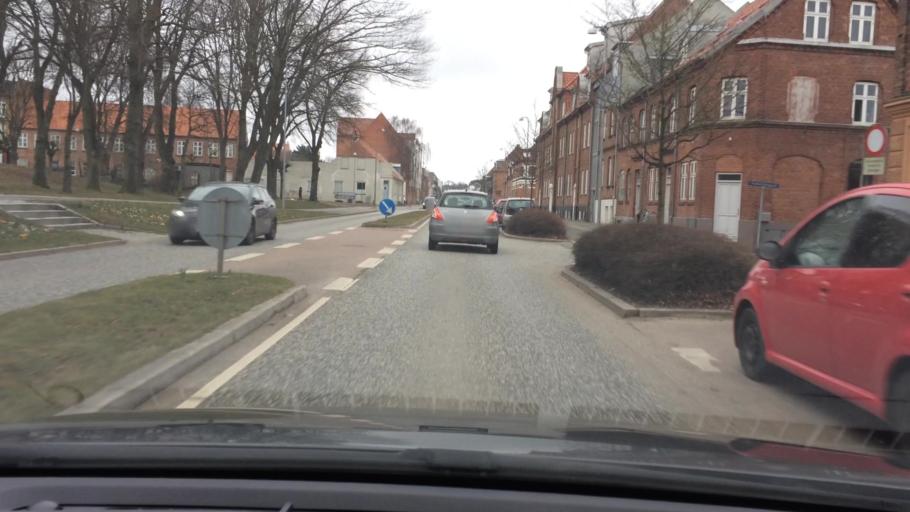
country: DK
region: Central Jutland
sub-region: Horsens Kommune
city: Horsens
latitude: 55.8712
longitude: 9.8350
